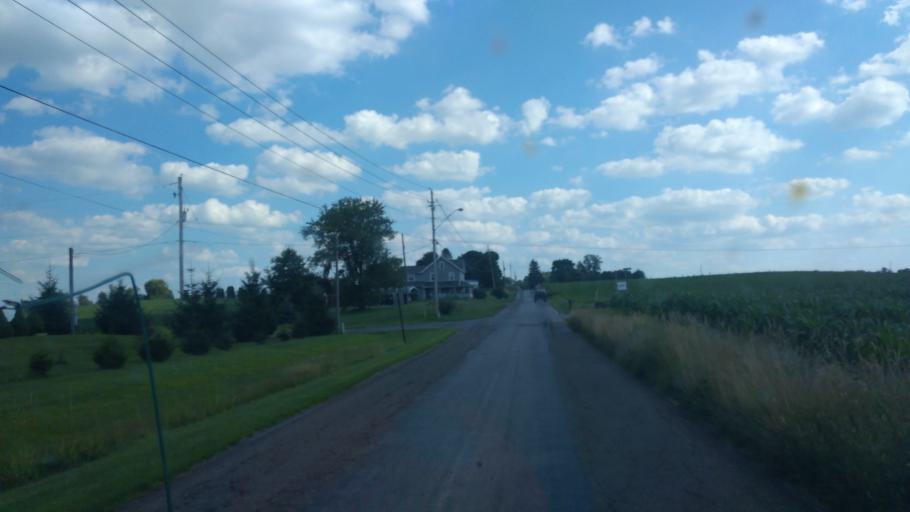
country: US
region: Ohio
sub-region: Wayne County
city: Apple Creek
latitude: 40.7514
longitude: -81.8438
